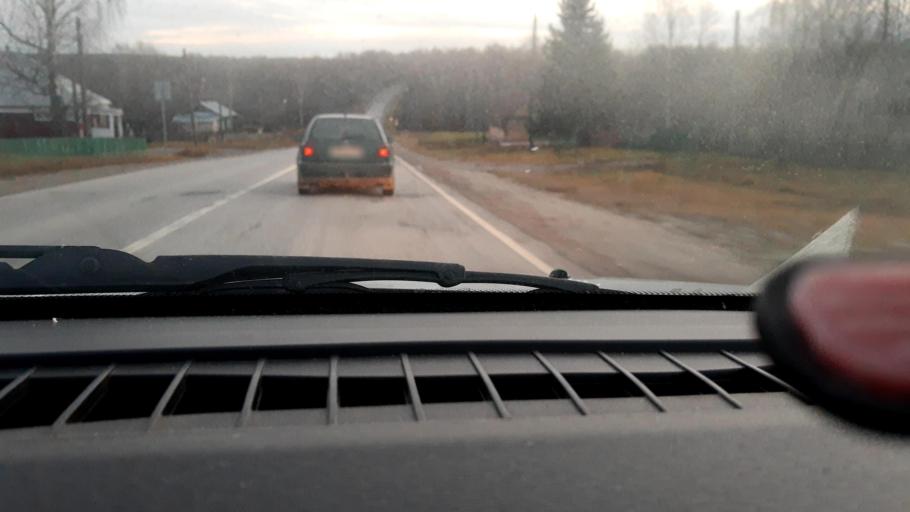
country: RU
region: Nizjnij Novgorod
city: Krasnyye Baki
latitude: 57.0658
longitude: 45.1375
